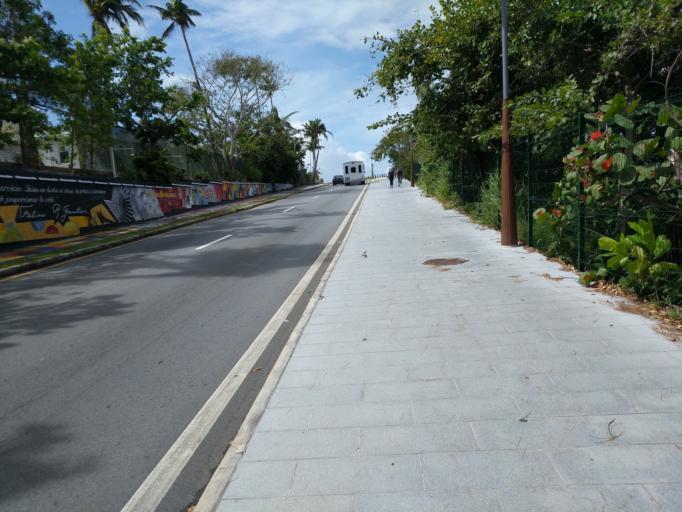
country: PR
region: San Juan
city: San Juan
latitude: 18.4660
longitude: -66.0935
